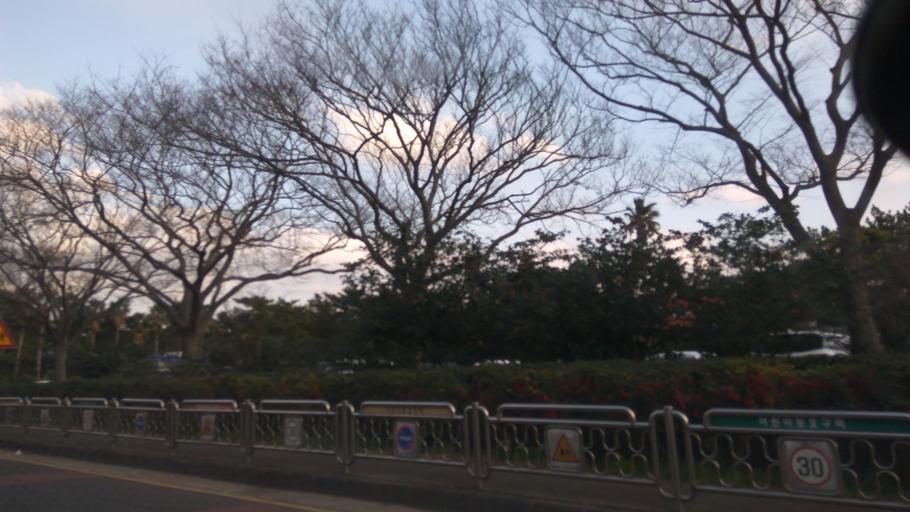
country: KR
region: Jeju-do
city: Gaigeturi
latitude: 33.3905
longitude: 126.2374
